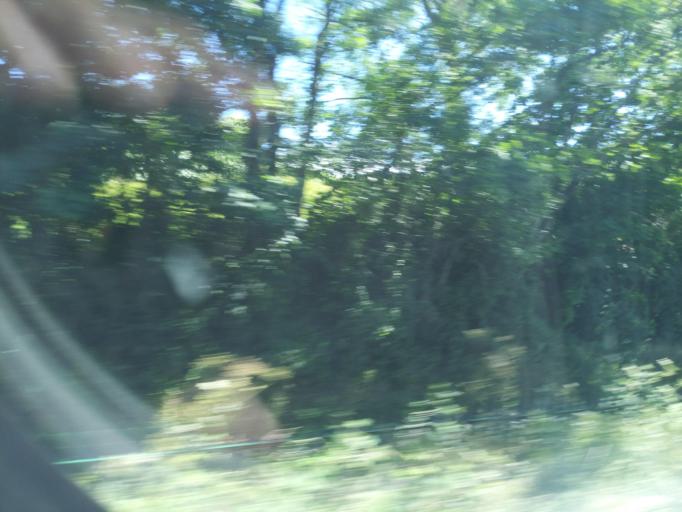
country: GB
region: England
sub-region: Cornwall
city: Saint Stephen
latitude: 50.3266
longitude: -4.8807
